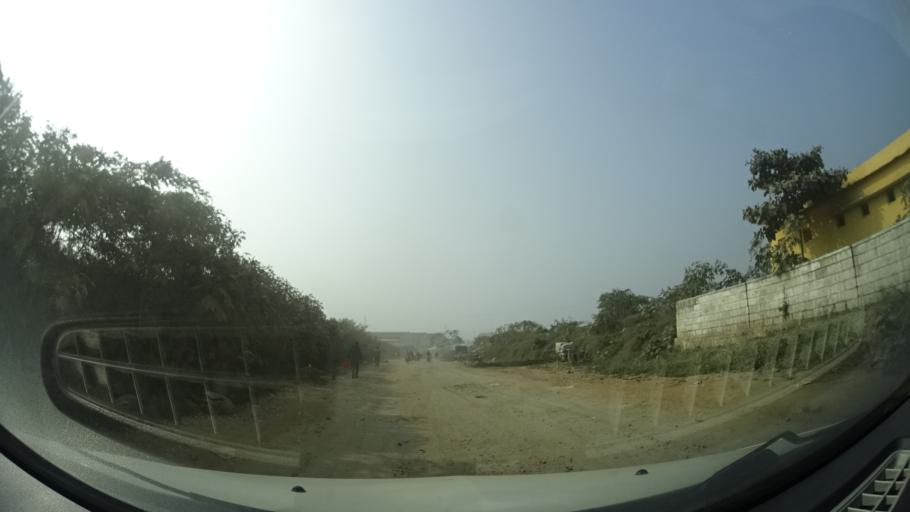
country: IN
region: Karnataka
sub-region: Bangalore Urban
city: Anekal
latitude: 12.8169
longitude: 77.6682
